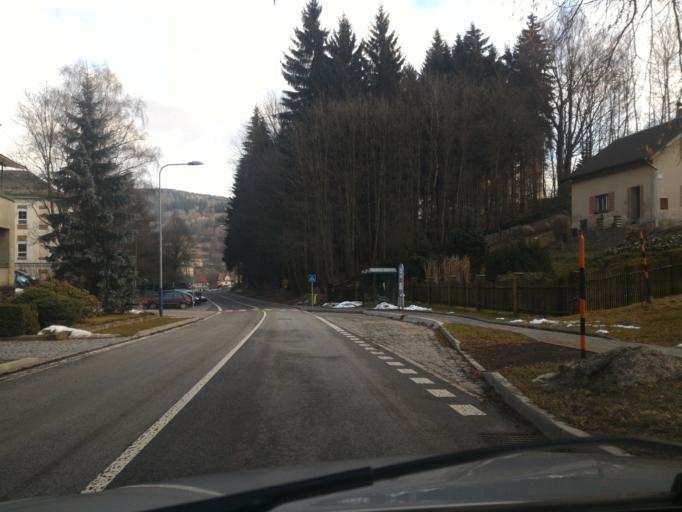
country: CZ
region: Liberecky
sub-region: Okres Jablonec nad Nisou
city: Tanvald
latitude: 50.7402
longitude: 15.2997
